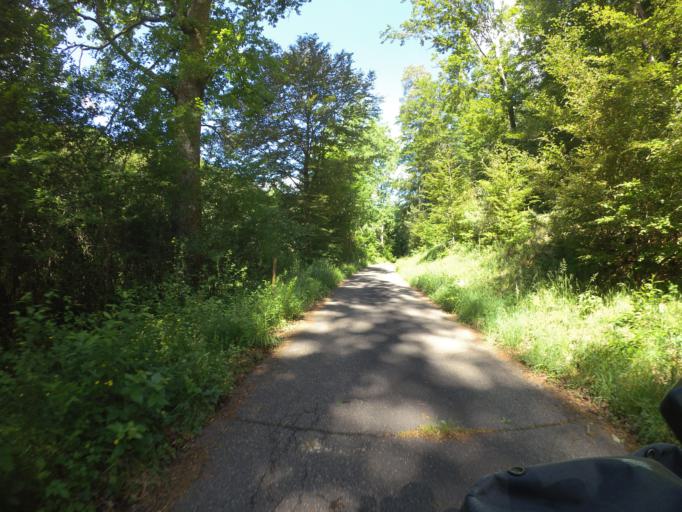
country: DE
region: Rheinland-Pfalz
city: Fischbach
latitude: 49.1004
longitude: 7.7054
